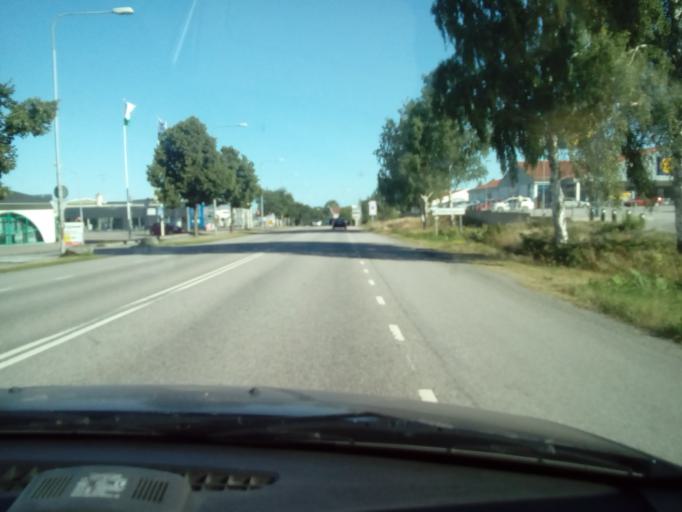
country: SE
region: Kalmar
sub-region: Vasterviks Kommun
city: Vaestervik
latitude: 57.7612
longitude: 16.6104
